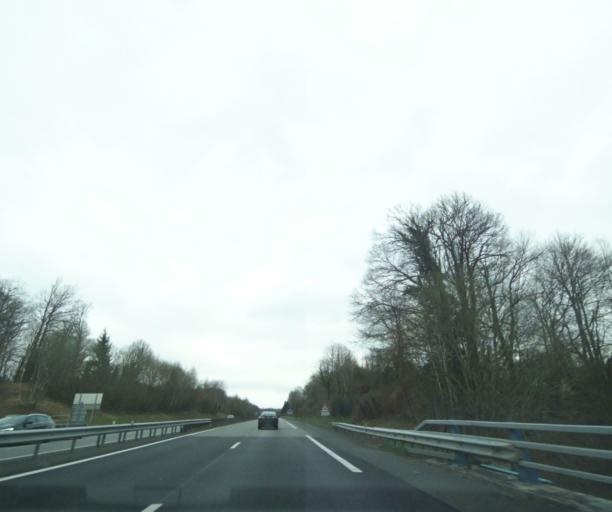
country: FR
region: Limousin
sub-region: Departement de la Correze
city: Uzerche
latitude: 45.3768
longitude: 1.5739
